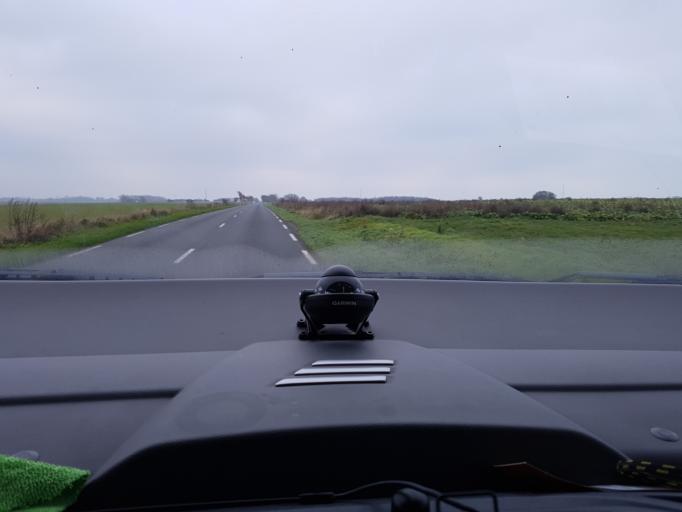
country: FR
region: Picardie
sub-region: Departement de la Somme
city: Ault
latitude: 50.1026
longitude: 1.4716
